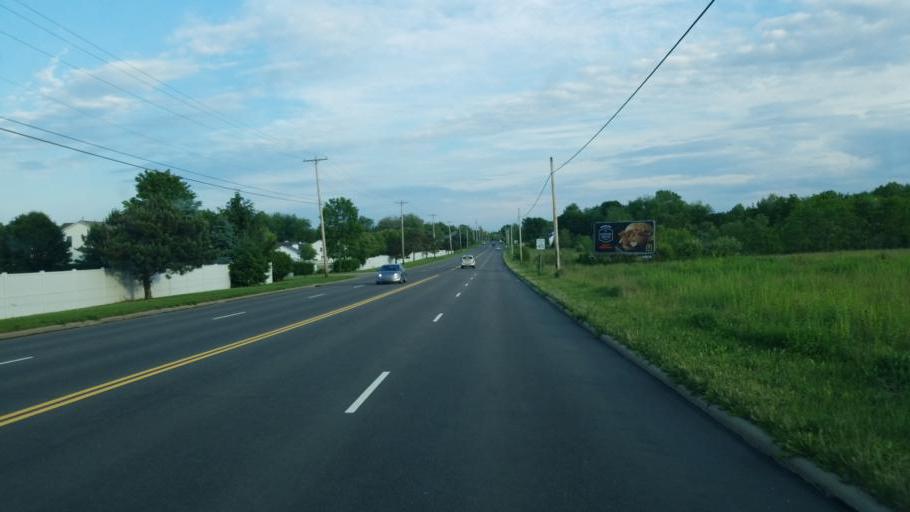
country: US
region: Ohio
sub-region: Stark County
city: Greentown
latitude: 40.9446
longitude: -81.4043
